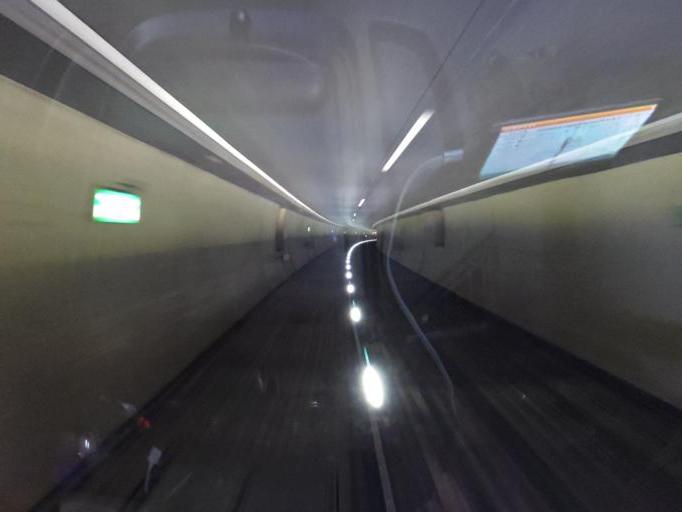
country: AT
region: Vorarlberg
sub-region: Politischer Bezirk Bregenz
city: Bregenz
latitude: 47.4927
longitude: 9.7530
